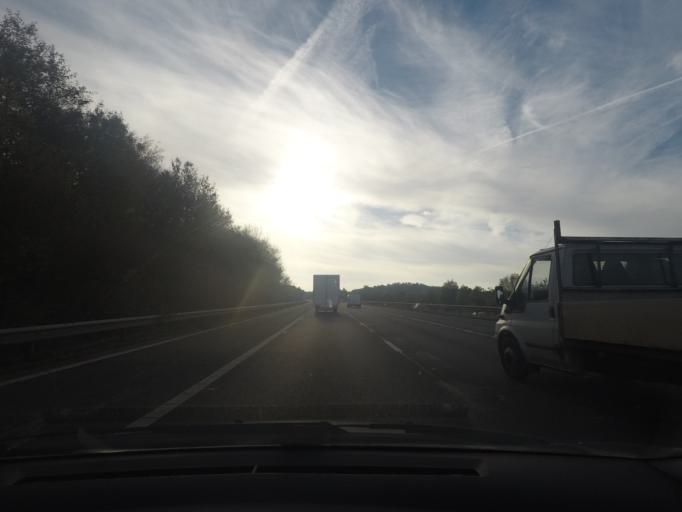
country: GB
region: England
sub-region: Barnsley
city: Dodworth
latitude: 53.5604
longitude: -1.5350
